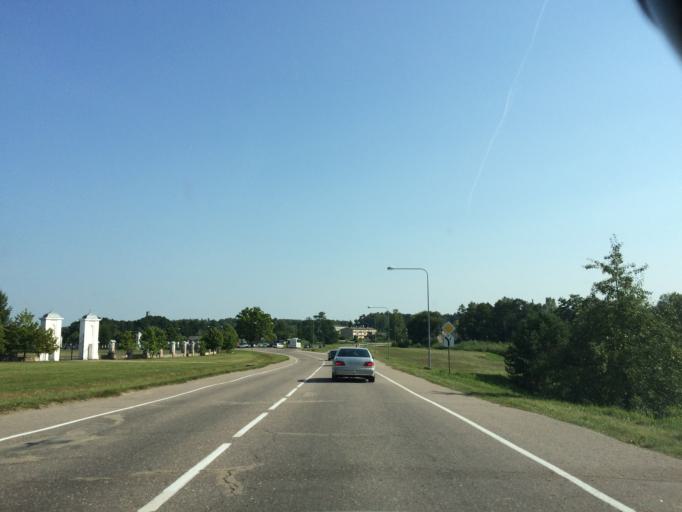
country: LV
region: Aglona
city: Aglona
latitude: 56.1272
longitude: 27.0105
